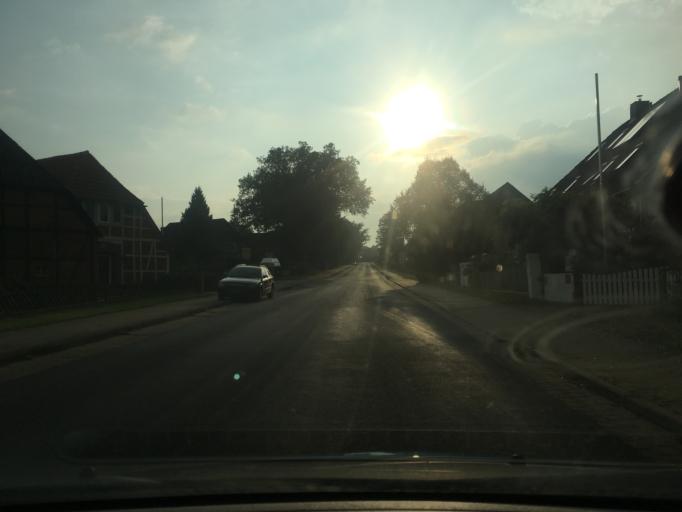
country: DE
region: Lower Saxony
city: Eyendorf
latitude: 53.2052
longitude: 10.1574
